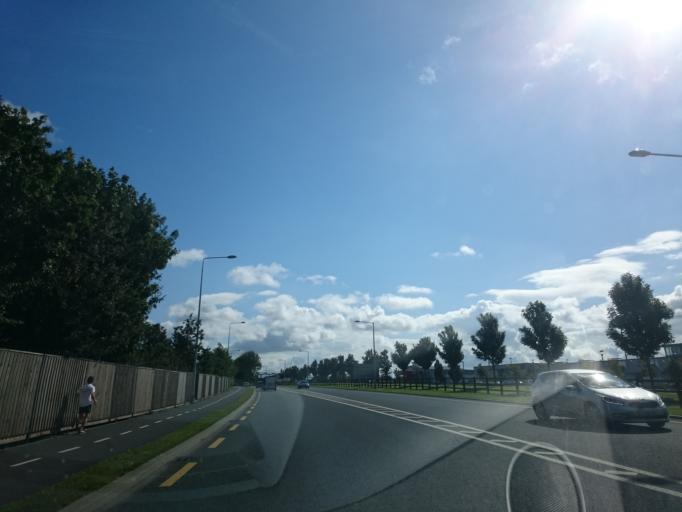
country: IE
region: Leinster
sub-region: Kilkenny
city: Kilkenny
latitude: 52.6357
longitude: -7.2483
